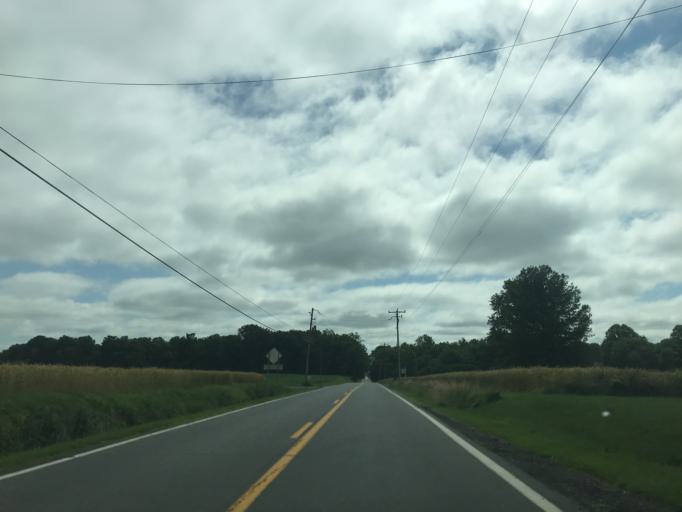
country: US
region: Maryland
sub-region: Caroline County
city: Ridgely
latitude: 38.8851
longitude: -75.9733
